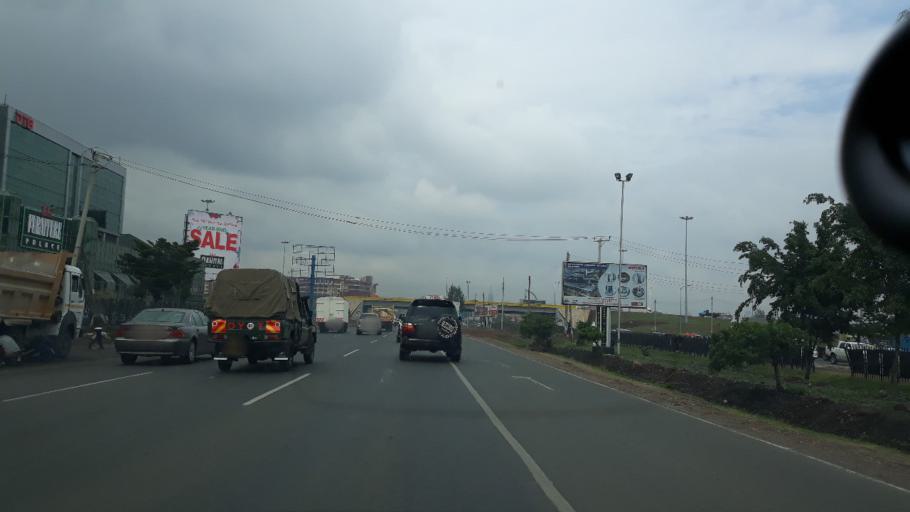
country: KE
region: Nairobi Area
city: Pumwani
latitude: -1.3263
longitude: 36.8493
